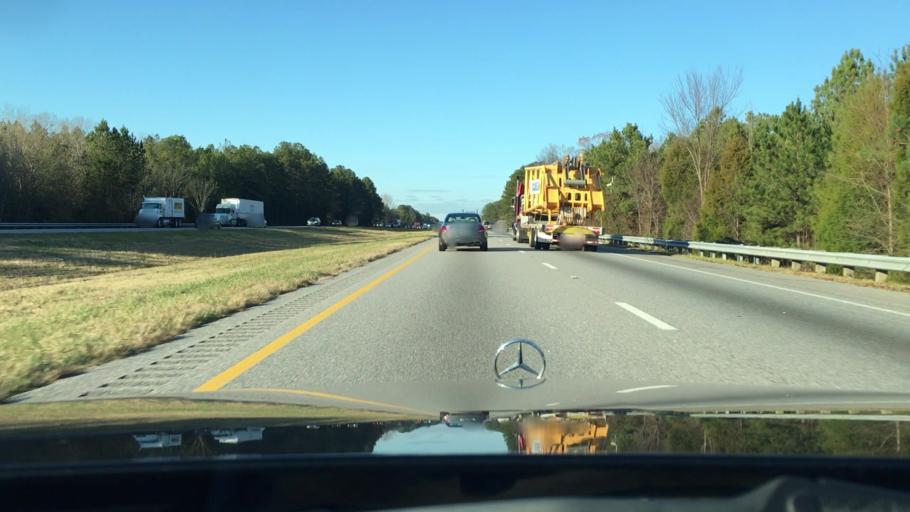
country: US
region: South Carolina
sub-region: Chester County
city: Great Falls
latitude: 34.6707
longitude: -81.0290
